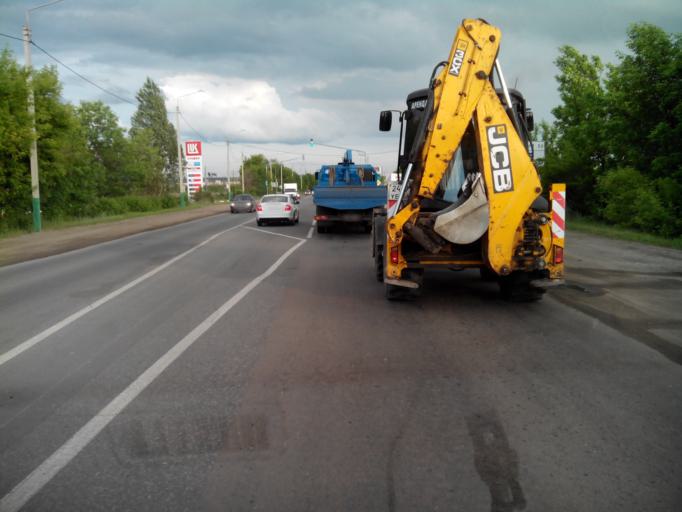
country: RU
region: Penza
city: Penza
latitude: 53.1390
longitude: 44.9678
